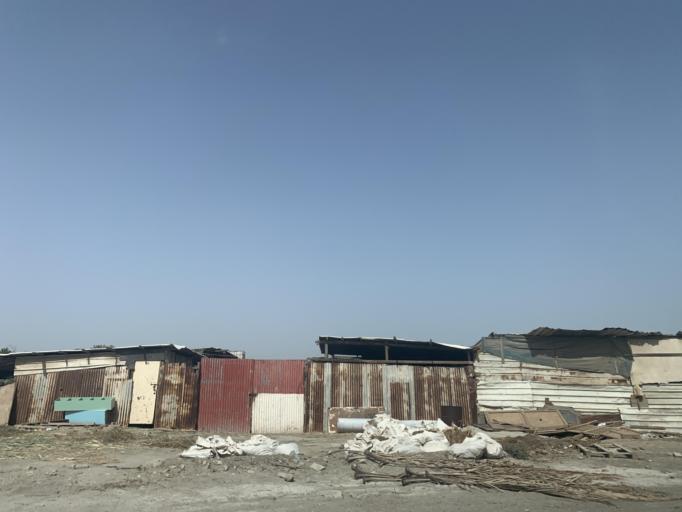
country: BH
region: Manama
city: Jidd Hafs
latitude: 26.2034
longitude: 50.5510
